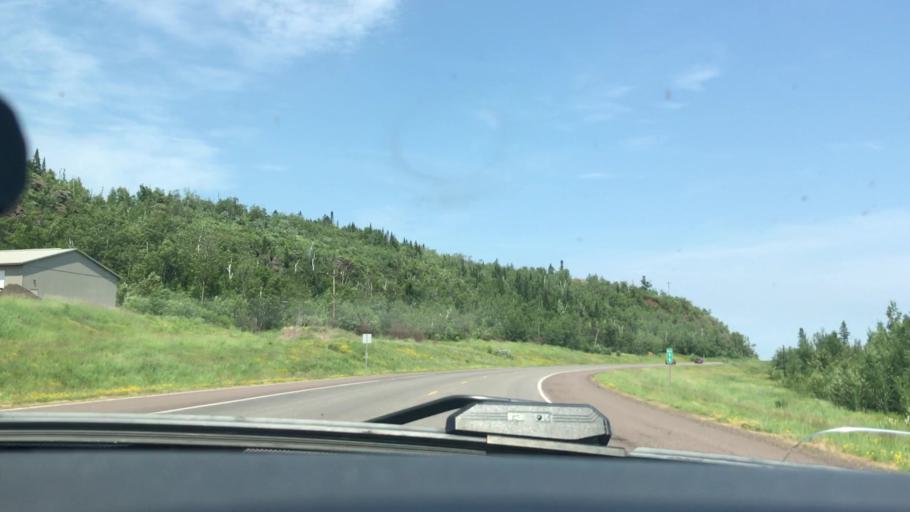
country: US
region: Minnesota
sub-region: Lake County
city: Silver Bay
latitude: 47.3022
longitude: -91.2506
